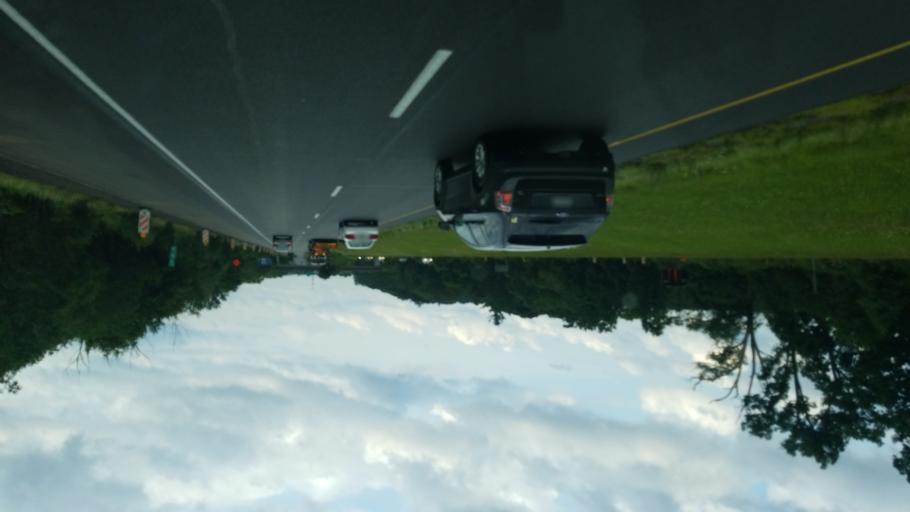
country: US
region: Pennsylvania
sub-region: Butler County
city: Fox Run
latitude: 40.7073
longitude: -80.1020
